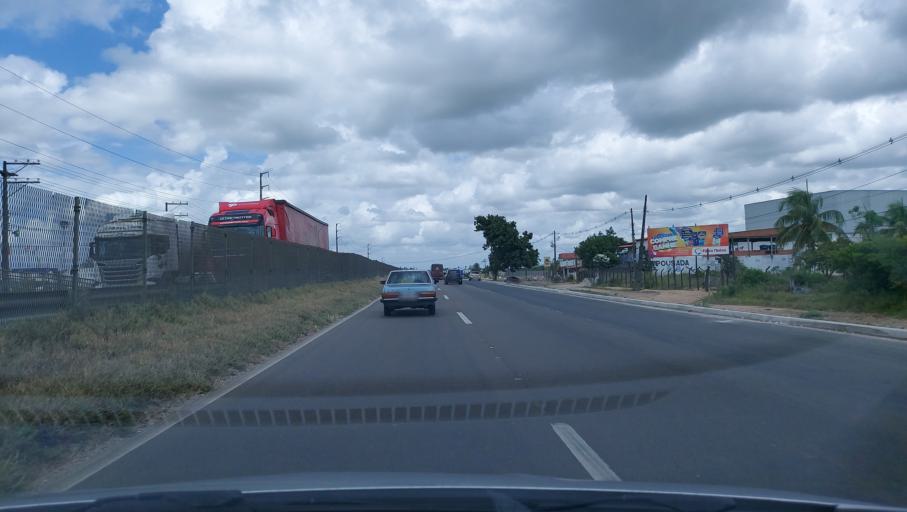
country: BR
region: Bahia
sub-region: Conceicao Do Jacuipe
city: Conceicao do Jacuipe
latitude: -12.3313
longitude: -38.8575
